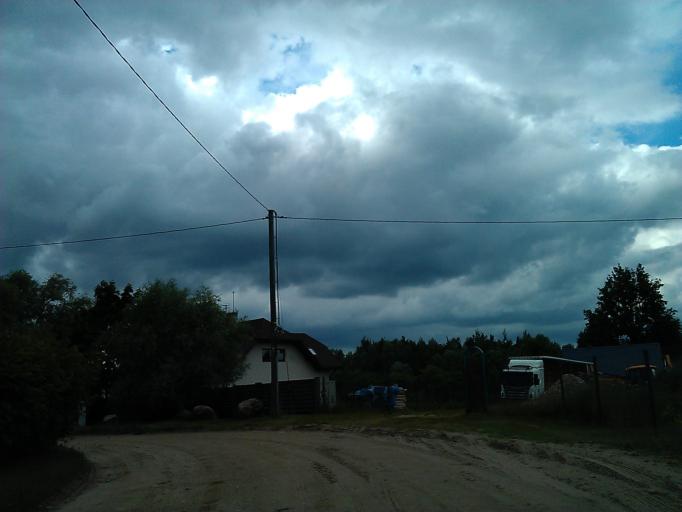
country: LV
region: Adazi
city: Adazi
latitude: 57.0795
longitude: 24.3135
